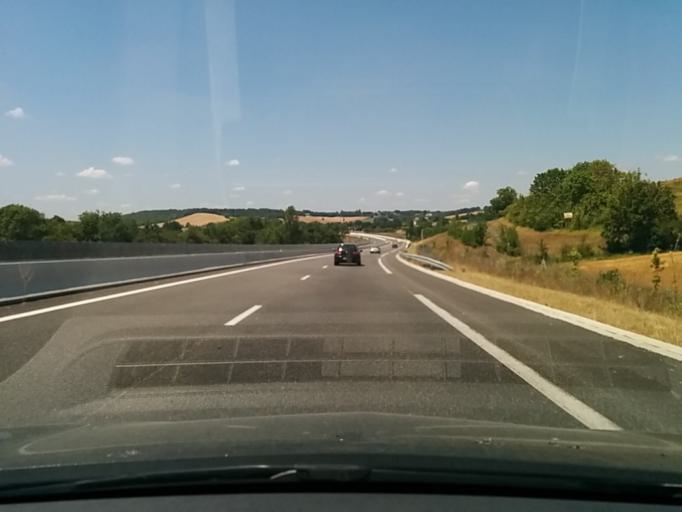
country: FR
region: Midi-Pyrenees
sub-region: Departement du Gers
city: Preignan
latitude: 43.6550
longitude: 0.6651
